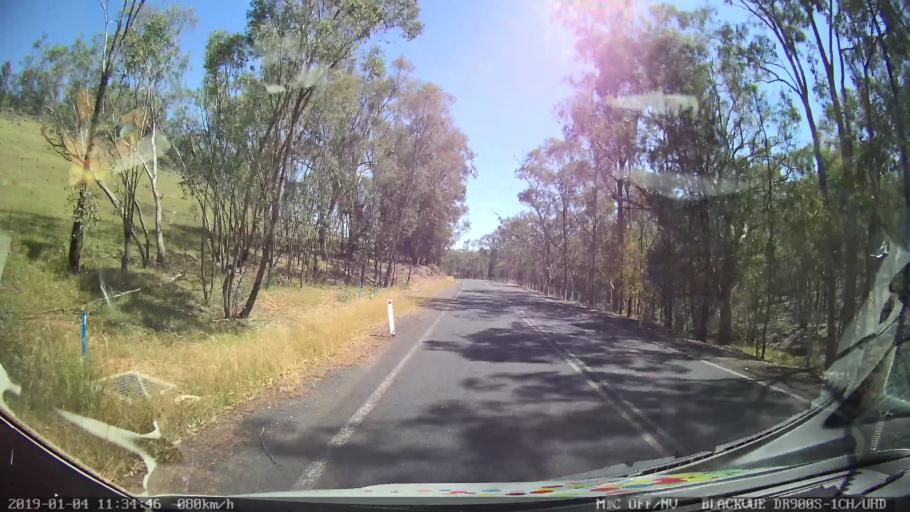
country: AU
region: New South Wales
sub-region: Cabonne
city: Molong
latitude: -33.0633
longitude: 148.8249
